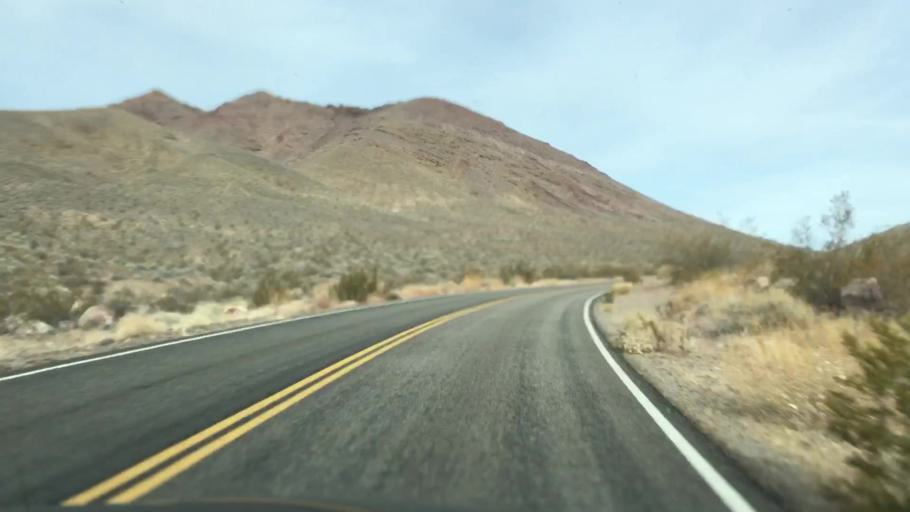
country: US
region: Nevada
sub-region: Nye County
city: Beatty
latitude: 36.7744
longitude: -116.9325
